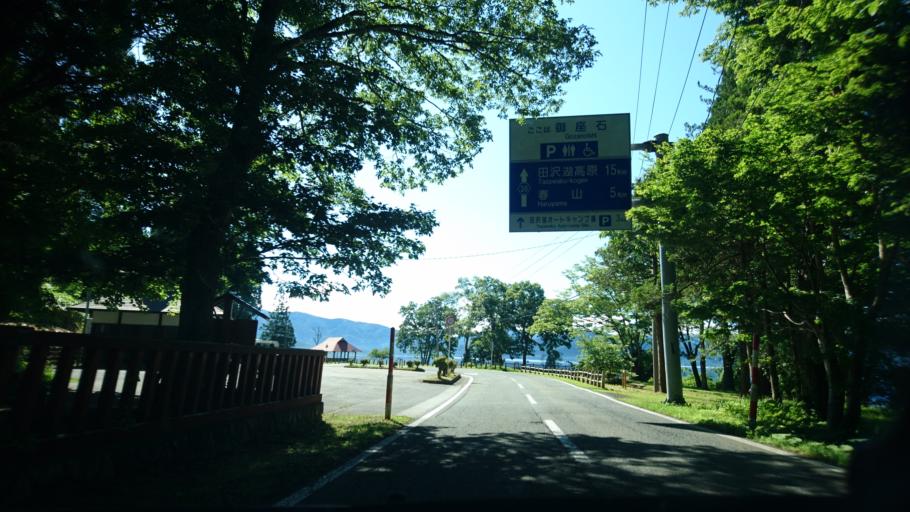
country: JP
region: Akita
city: Kakunodatemachi
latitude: 39.7515
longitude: 140.6490
